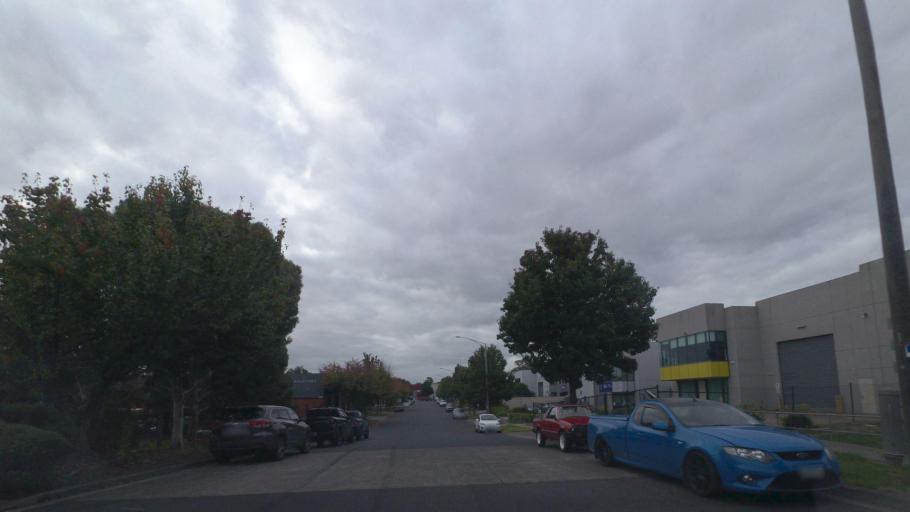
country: AU
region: Victoria
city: Forest Hill
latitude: -37.8350
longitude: 145.1862
